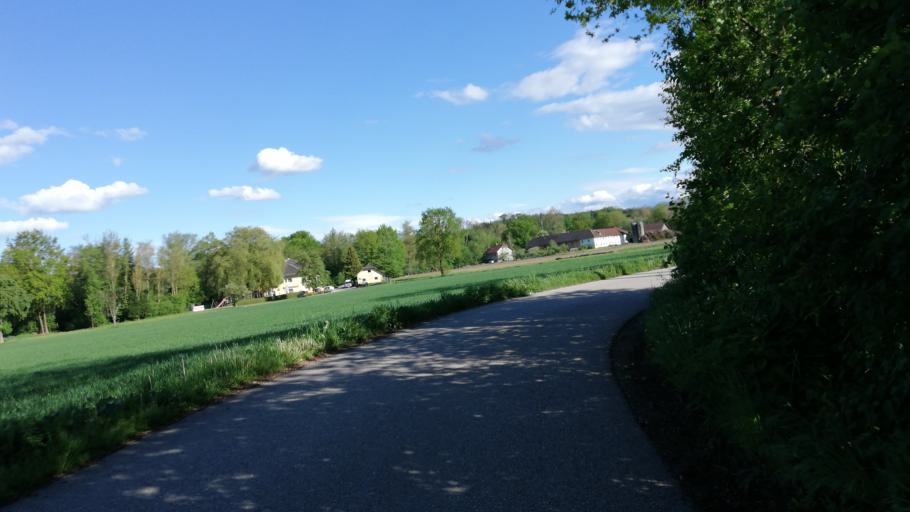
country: AT
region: Upper Austria
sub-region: Politischer Bezirk Grieskirchen
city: Bad Schallerbach
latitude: 48.2116
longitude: 13.9295
